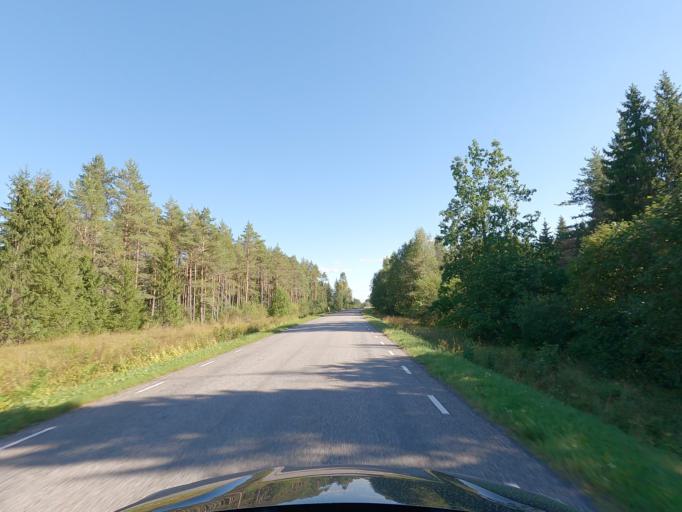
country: EE
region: Raplamaa
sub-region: Kohila vald
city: Kohila
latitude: 59.1237
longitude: 24.6745
